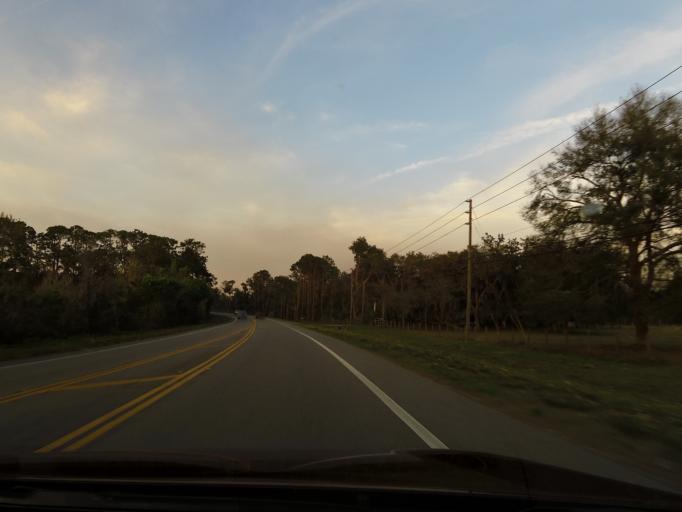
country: US
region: Florida
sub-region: Volusia County
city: North DeLand
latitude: 29.0913
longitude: -81.2979
